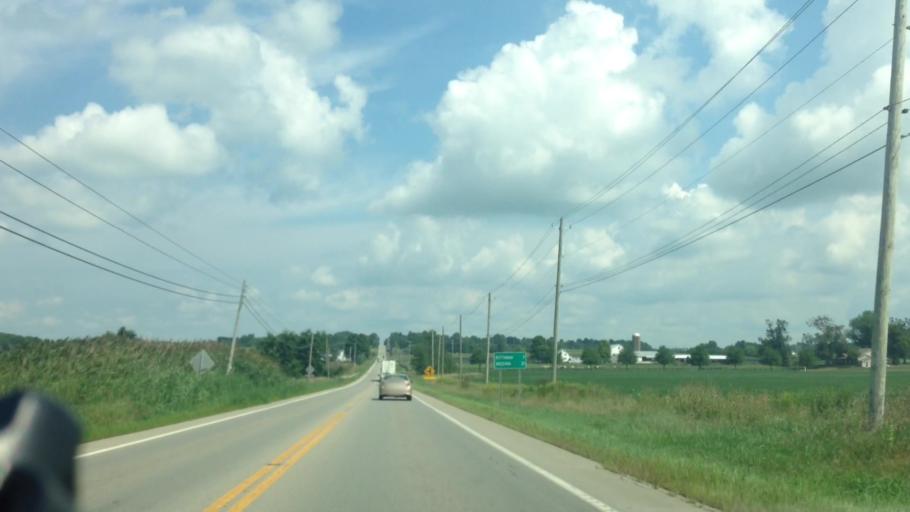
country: US
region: Ohio
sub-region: Wayne County
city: Orrville
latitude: 40.8702
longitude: -81.7634
